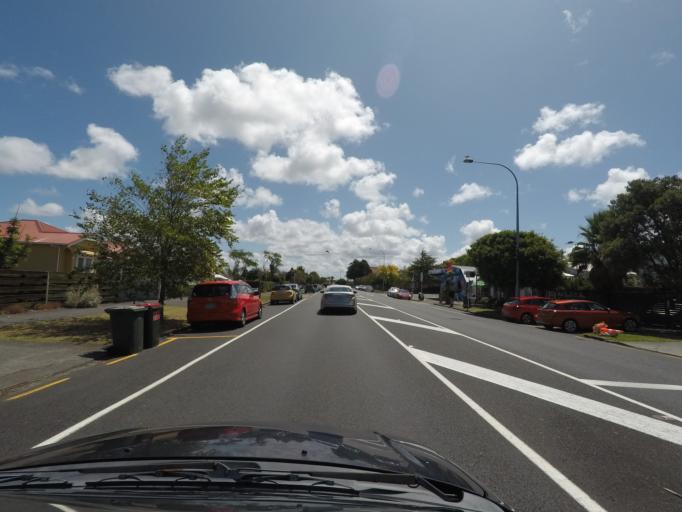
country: NZ
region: Auckland
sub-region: Auckland
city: Auckland
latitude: -36.8595
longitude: 174.7237
